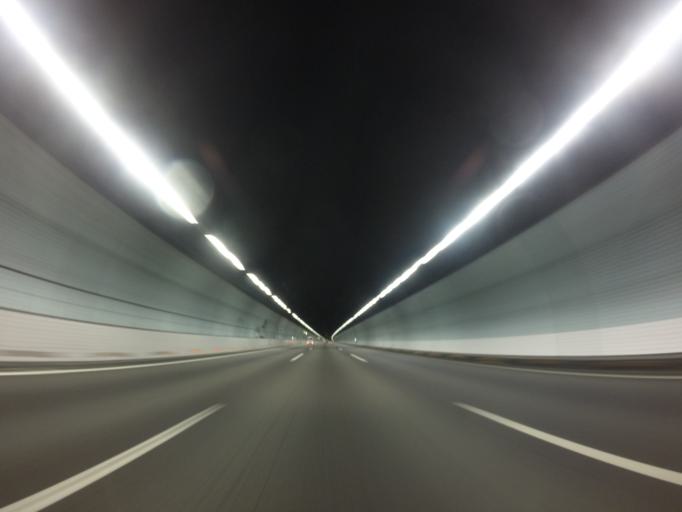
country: JP
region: Shizuoka
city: Yaizu
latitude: 34.9074
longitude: 138.3401
